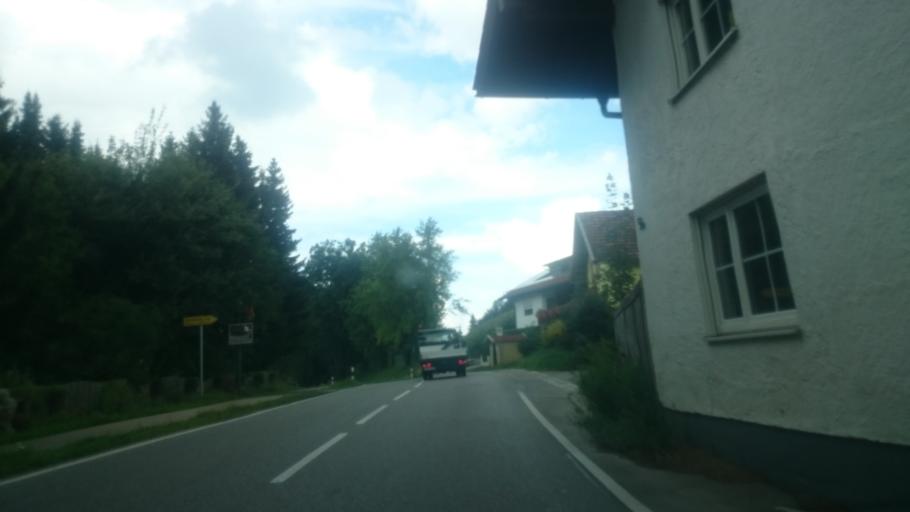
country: DE
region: Bavaria
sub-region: Swabia
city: Obergunzburg
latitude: 47.8312
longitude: 10.4304
